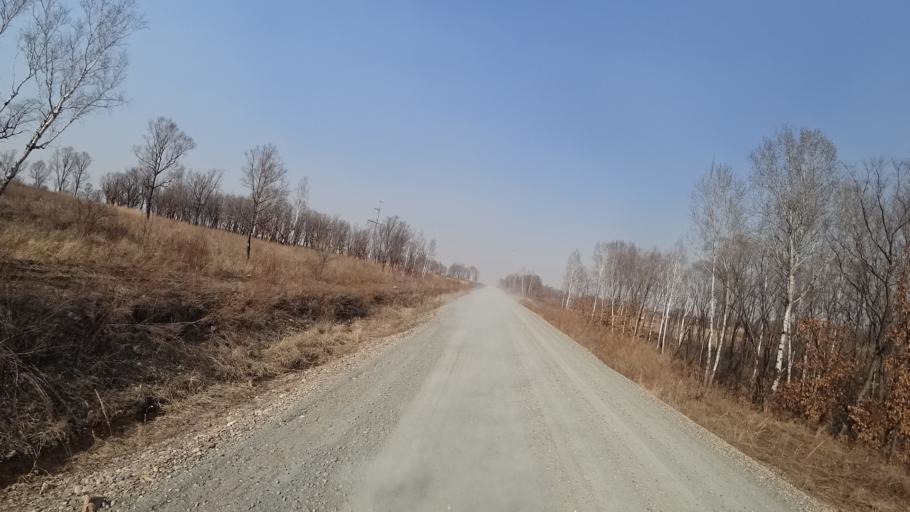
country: RU
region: Amur
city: Novobureyskiy
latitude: 49.8012
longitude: 129.9603
